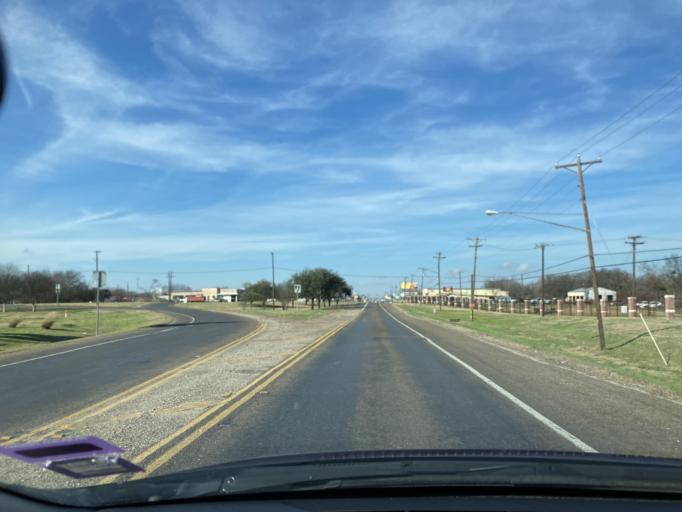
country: US
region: Texas
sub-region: Navarro County
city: Corsicana
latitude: 32.0829
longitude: -96.4516
